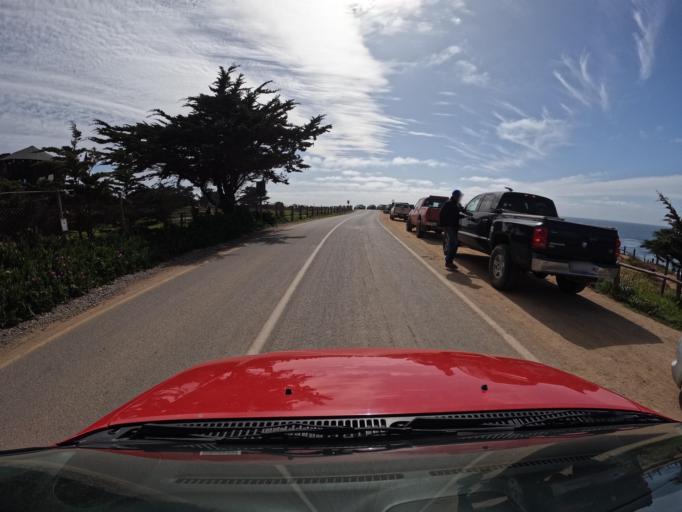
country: CL
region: O'Higgins
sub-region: Provincia de Colchagua
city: Santa Cruz
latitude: -34.4259
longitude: -72.0443
